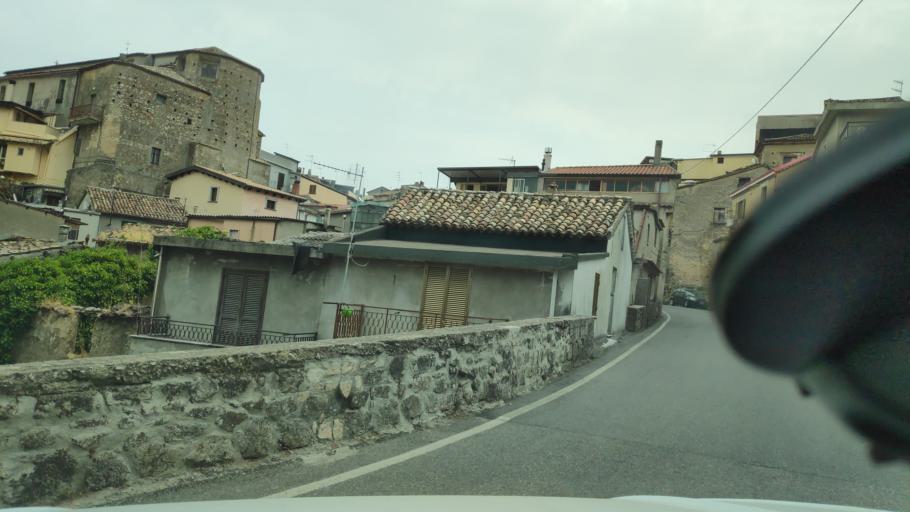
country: IT
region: Calabria
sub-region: Provincia di Catanzaro
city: Davoli
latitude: 38.6504
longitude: 16.4850
